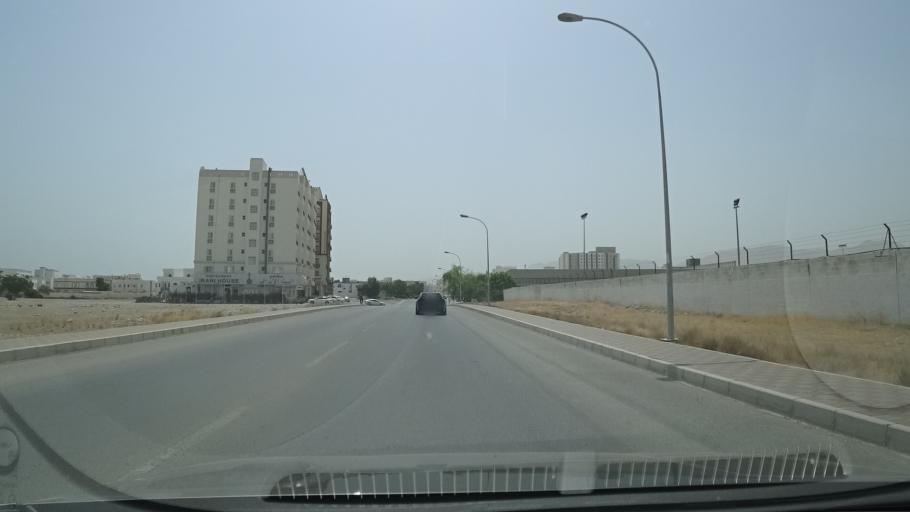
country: OM
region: Muhafazat Masqat
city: Bawshar
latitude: 23.5924
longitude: 58.3727
